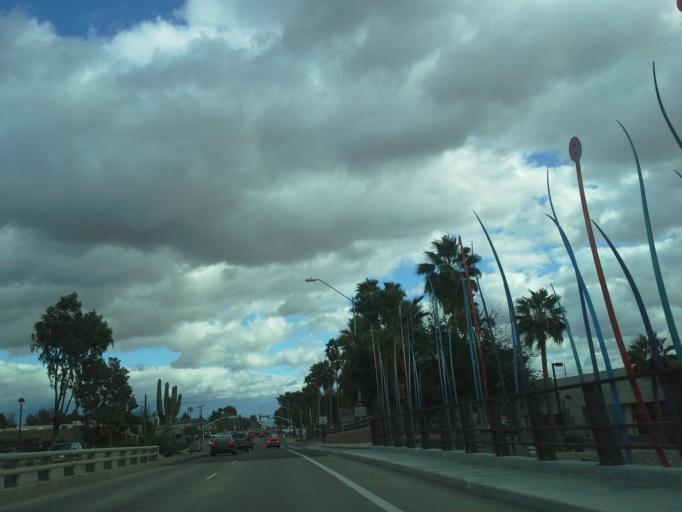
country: US
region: Arizona
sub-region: Maricopa County
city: Scottsdale
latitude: 33.4803
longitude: -111.9118
